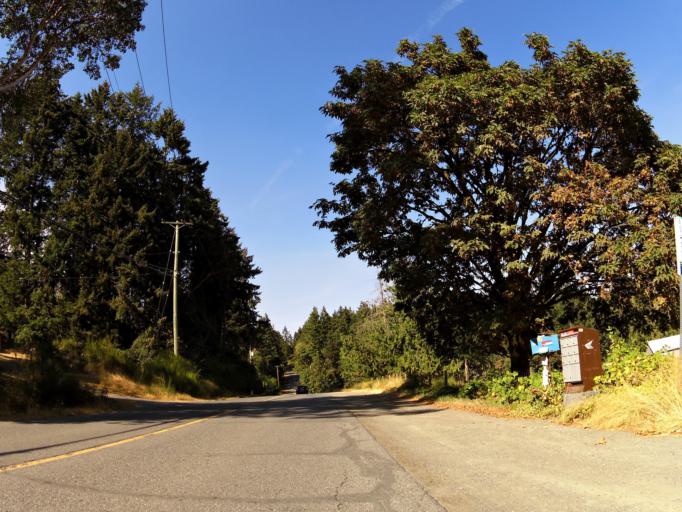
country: CA
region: British Columbia
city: North Saanich
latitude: 48.6796
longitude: -123.5506
